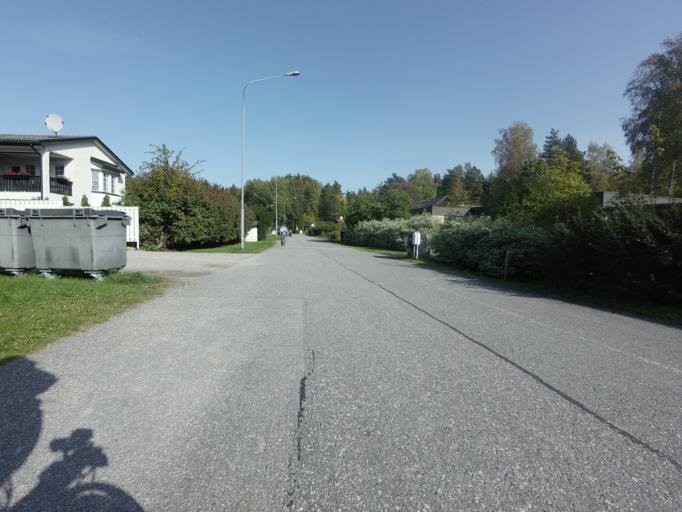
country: FI
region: Uusimaa
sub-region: Helsinki
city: Espoo
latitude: 60.1798
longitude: 24.6583
